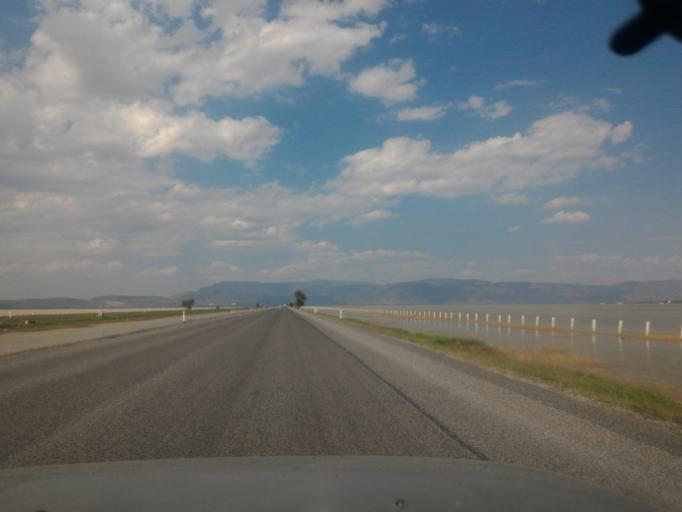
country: MX
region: Jalisco
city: Atoyac
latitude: 20.0606
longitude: -103.5223
